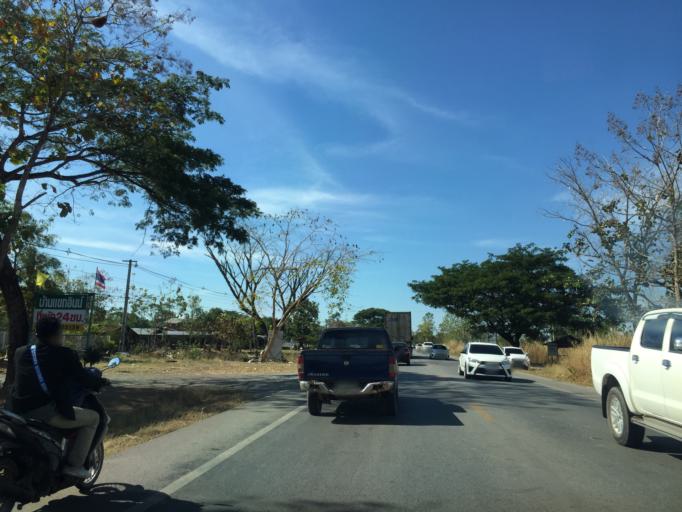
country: TH
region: Changwat Nong Bua Lamphu
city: Na Klang
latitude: 17.3170
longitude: 102.1581
